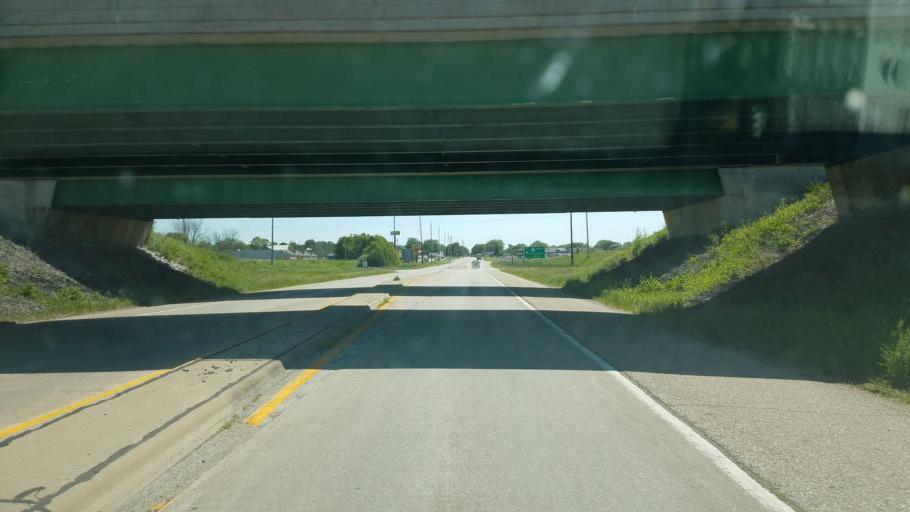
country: US
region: Illinois
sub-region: McLean County
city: Heyworth
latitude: 40.3120
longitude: -88.9901
